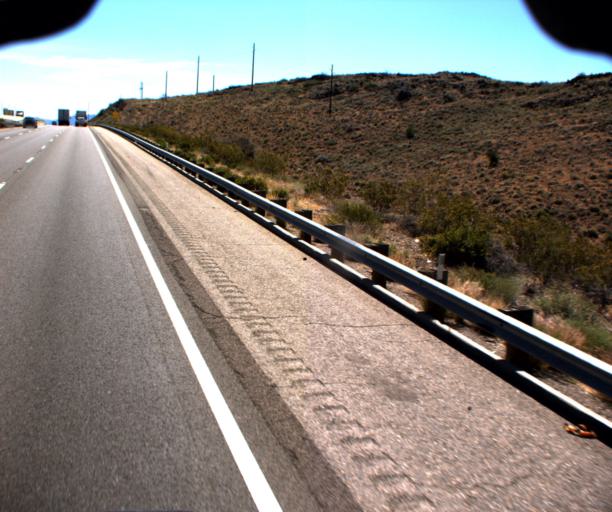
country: US
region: Arizona
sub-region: Mohave County
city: Kingman
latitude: 35.2101
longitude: -114.1068
